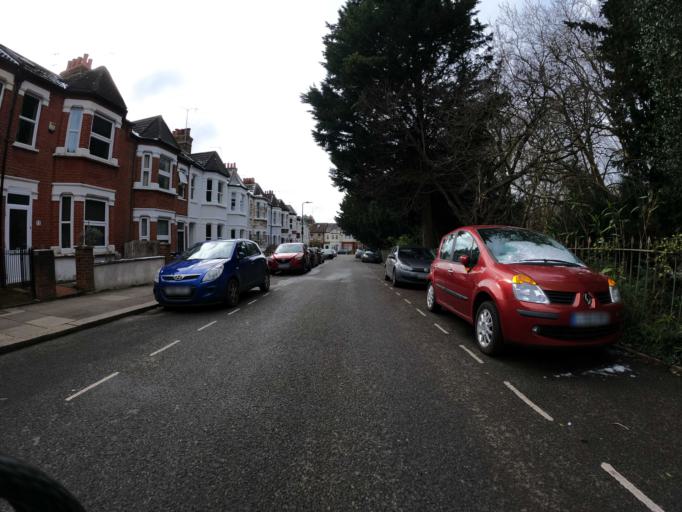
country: GB
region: England
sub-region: Greater London
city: Greenford
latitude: 51.5105
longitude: -0.3412
